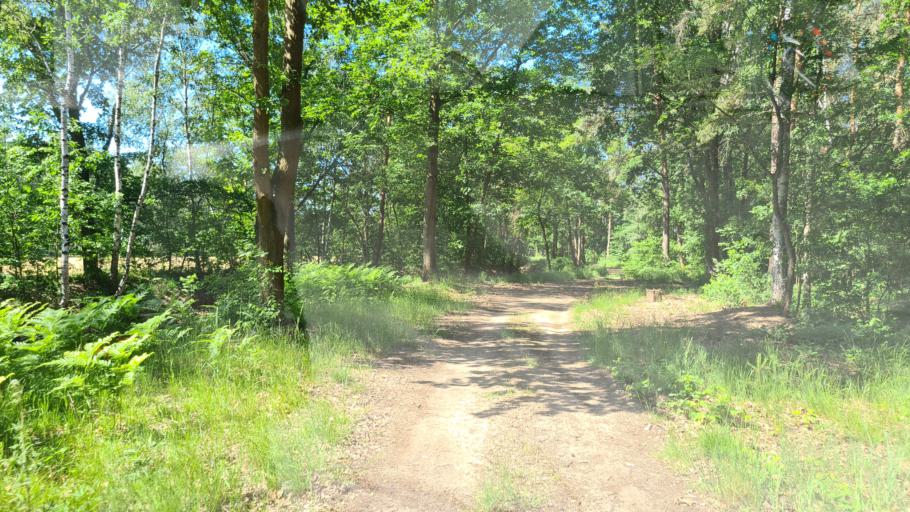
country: DE
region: Brandenburg
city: Plessa
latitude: 51.4710
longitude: 13.6544
